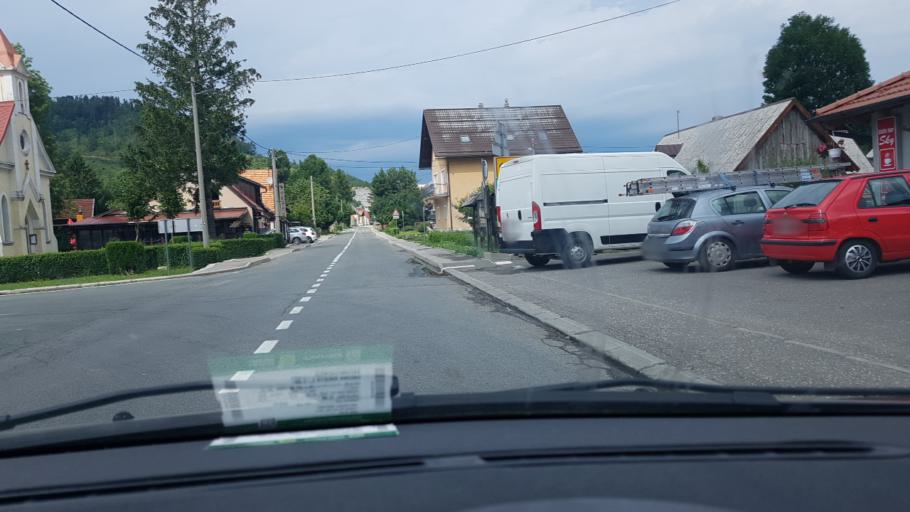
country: HR
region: Primorsko-Goranska
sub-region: Grad Delnice
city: Delnice
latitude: 45.3167
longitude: 14.7287
